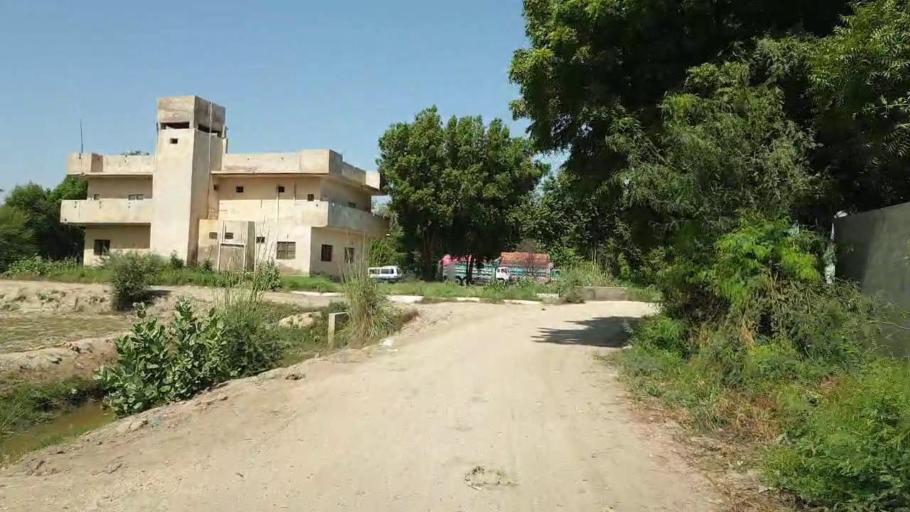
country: PK
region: Sindh
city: Hyderabad
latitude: 25.4799
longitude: 68.4096
